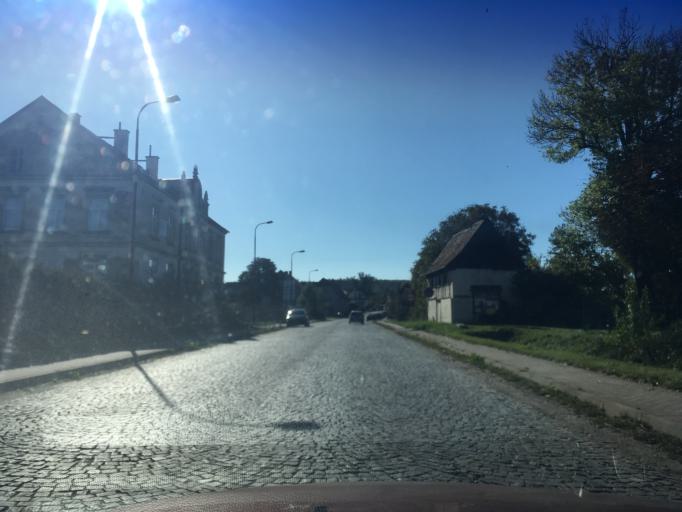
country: DE
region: Saxony
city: Zittau
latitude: 50.8985
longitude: 14.8444
